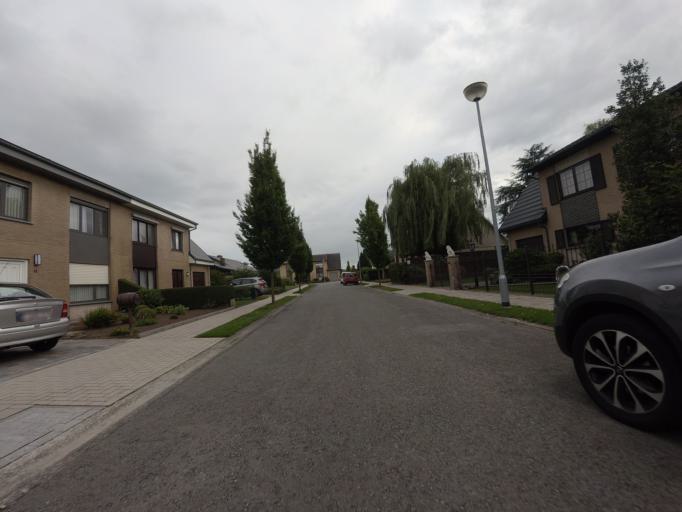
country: BE
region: Flanders
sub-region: Provincie Antwerpen
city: Willebroek
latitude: 51.0379
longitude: 4.3440
